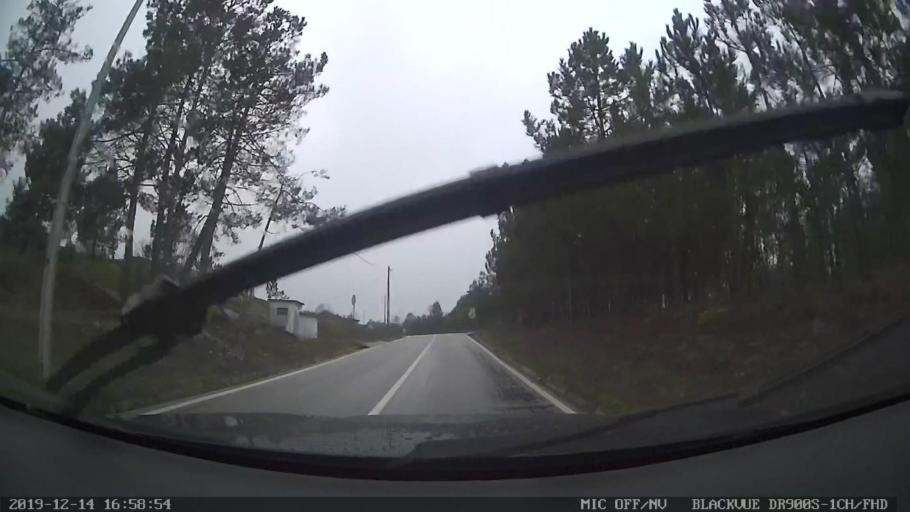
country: PT
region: Vila Real
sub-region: Murca
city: Murca
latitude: 41.4354
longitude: -7.5563
